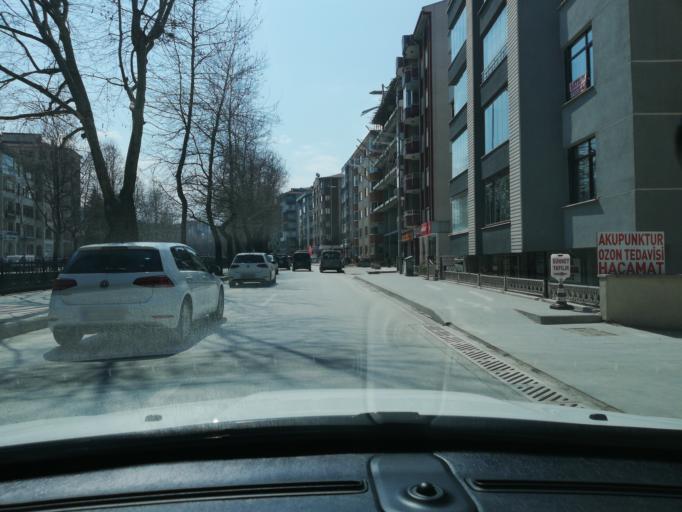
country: TR
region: Kastamonu
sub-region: Cide
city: Kastamonu
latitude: 41.3880
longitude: 33.7798
